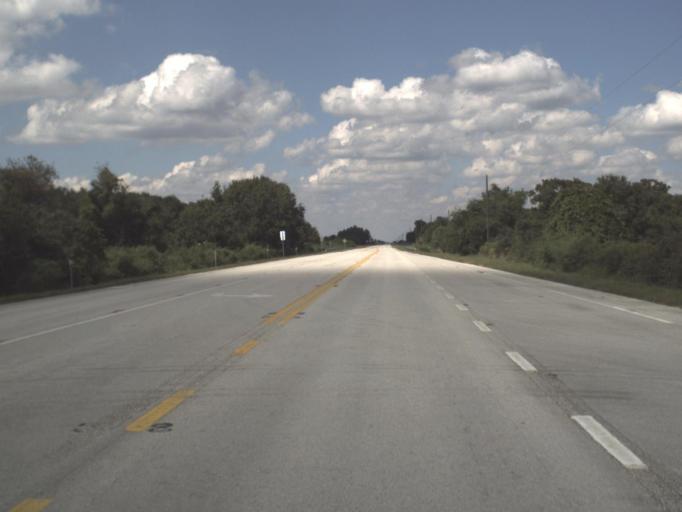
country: US
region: Florida
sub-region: Highlands County
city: Lake Placid
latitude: 27.4001
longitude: -81.1642
